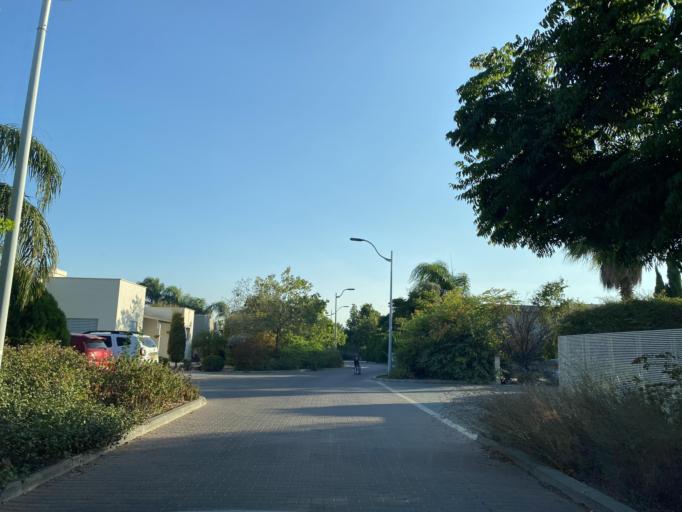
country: IL
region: Northern District
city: Qiryat Shemona
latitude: 33.1757
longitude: 35.6051
